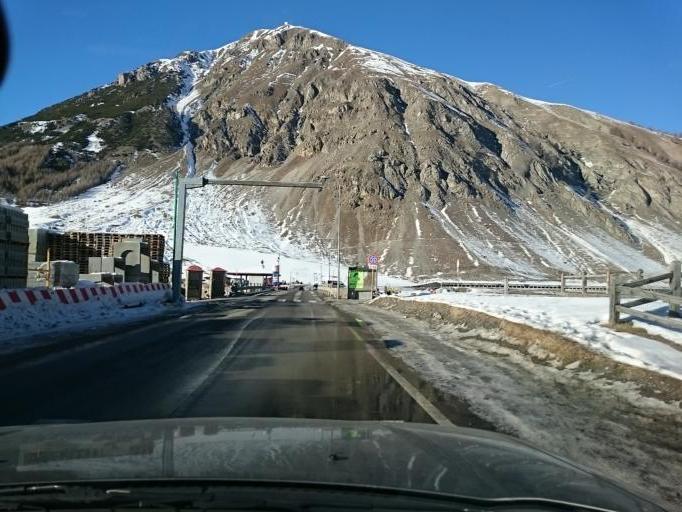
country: IT
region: Lombardy
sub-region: Provincia di Sondrio
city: Livigno
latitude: 46.5554
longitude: 10.1452
